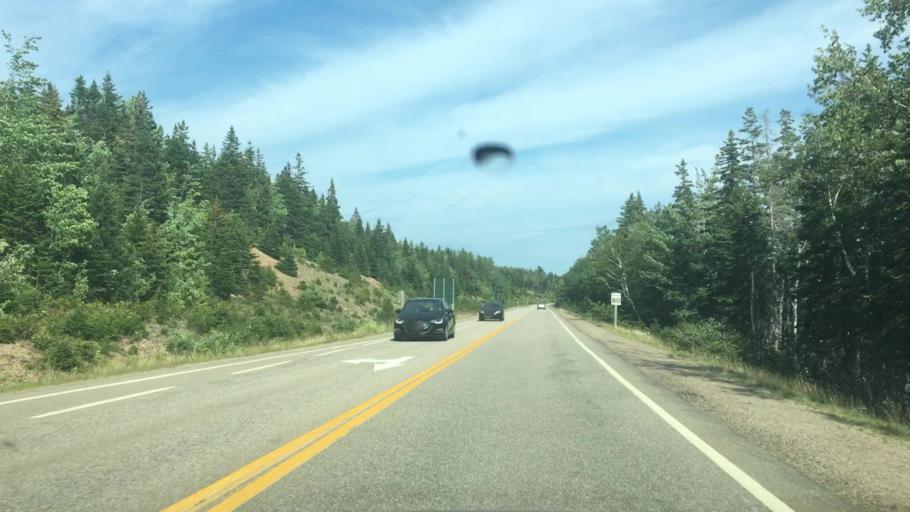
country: CA
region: Nova Scotia
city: Sydney Mines
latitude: 46.7127
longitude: -60.3633
